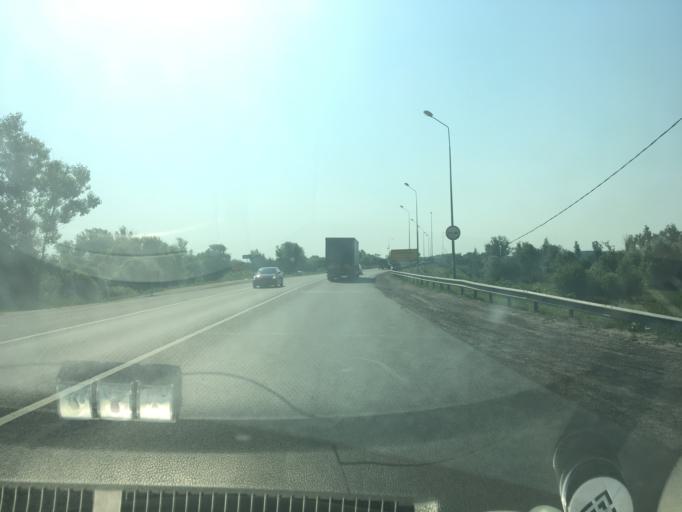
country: RU
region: Nizjnij Novgorod
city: Kstovo
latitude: 56.0997
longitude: 44.3065
